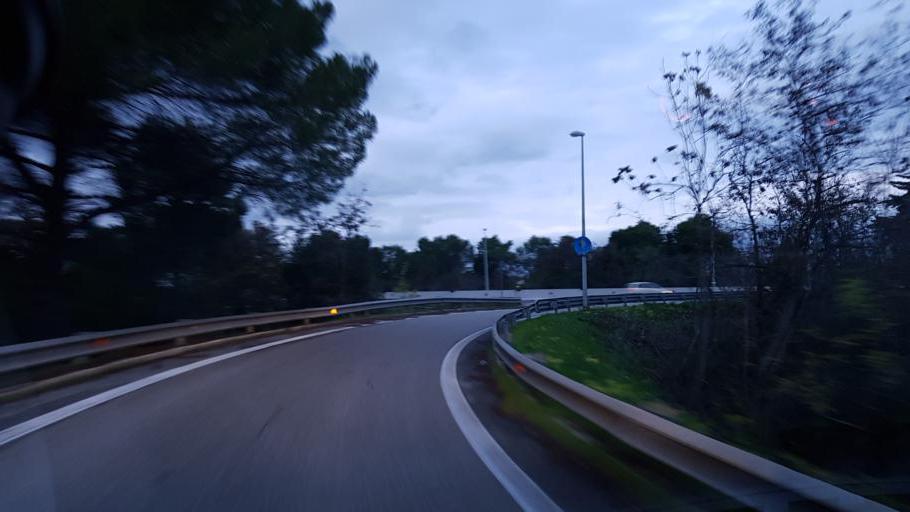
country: IT
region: Apulia
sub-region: Provincia di Taranto
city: Paolo VI
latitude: 40.5044
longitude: 17.2635
